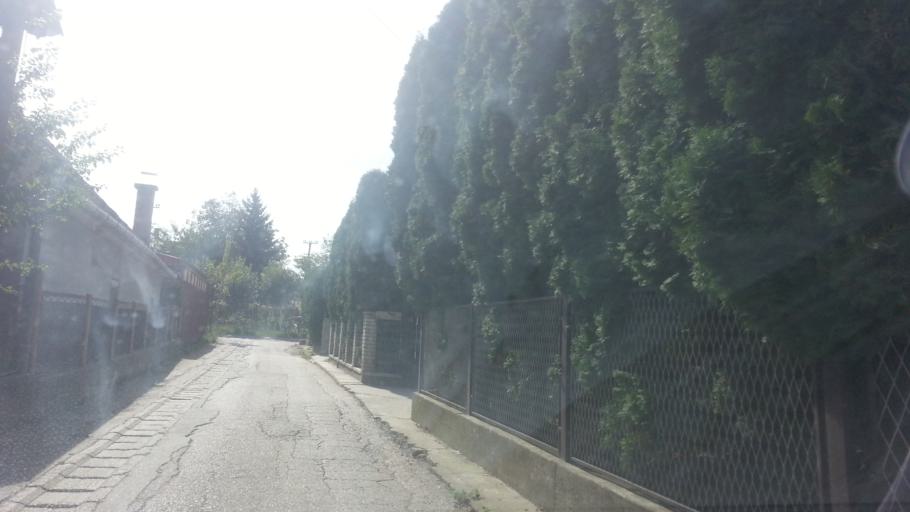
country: RS
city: Novi Banovci
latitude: 44.9486
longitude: 20.2818
